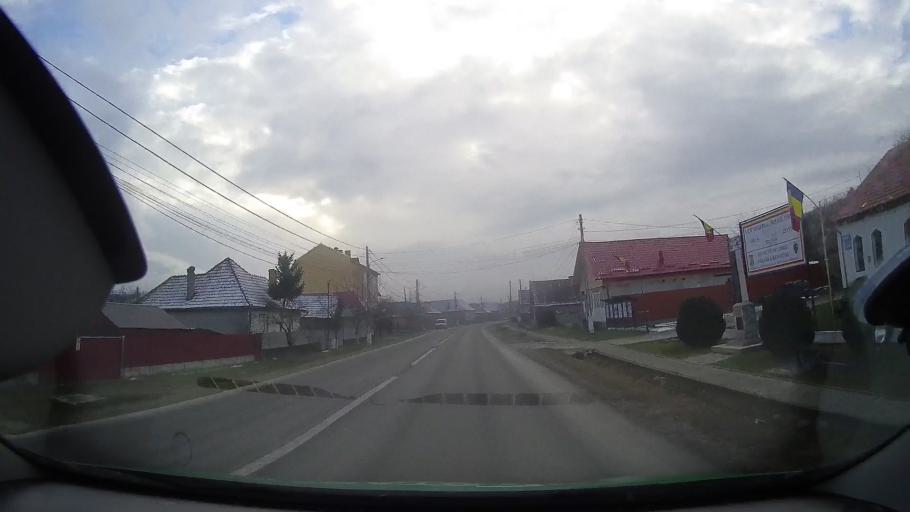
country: RO
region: Mures
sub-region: Comuna Cucerdea
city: Cucerdea
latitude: 46.4048
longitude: 24.2643
